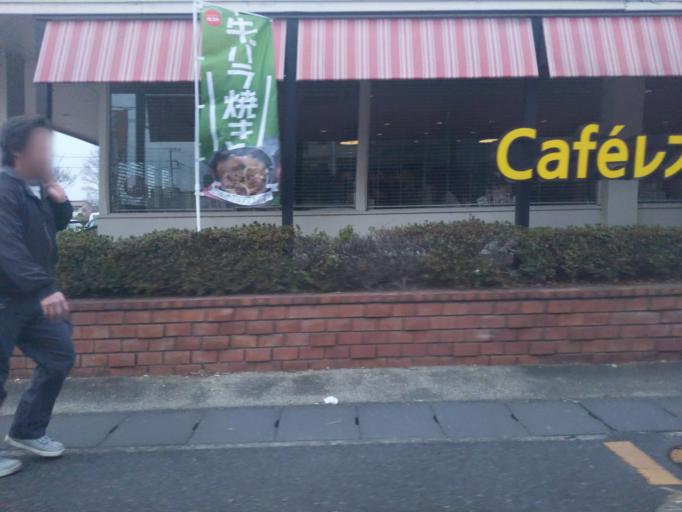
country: JP
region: Saitama
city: Koshigaya
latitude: 35.8588
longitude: 139.7970
